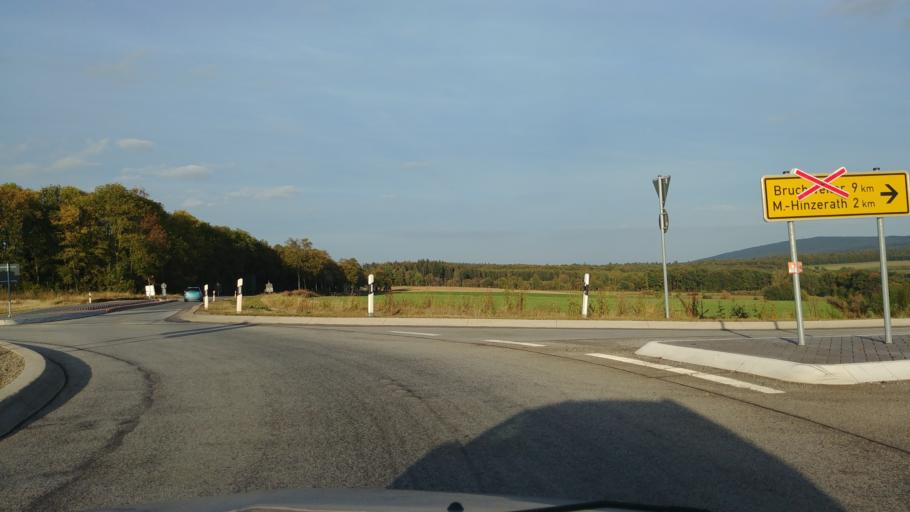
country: DE
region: Rheinland-Pfalz
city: Kommen
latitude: 49.8538
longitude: 7.1639
